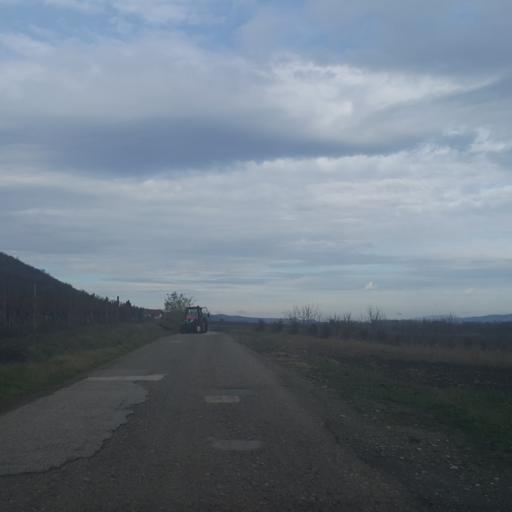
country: RS
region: Central Serbia
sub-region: Zajecarski Okrug
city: Knjazevac
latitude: 43.6185
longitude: 22.2611
